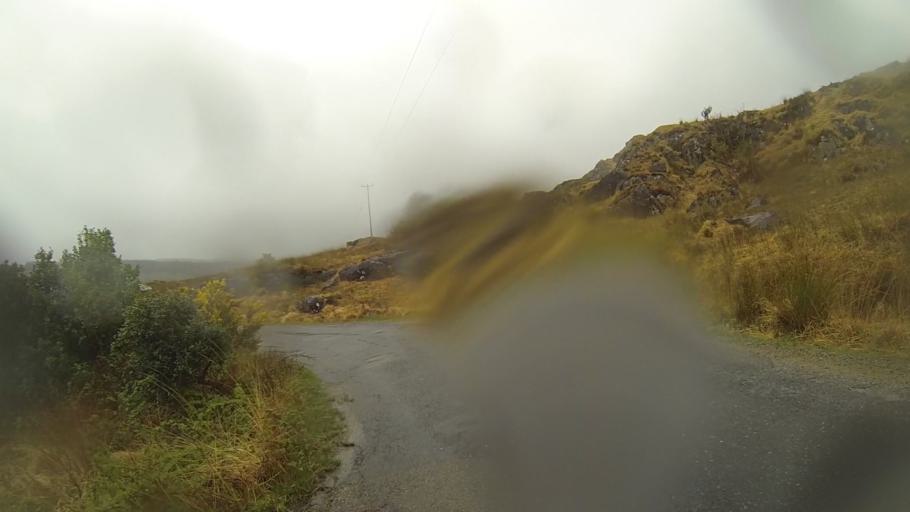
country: IE
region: Munster
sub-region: Ciarrai
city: Kenmare
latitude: 51.9599
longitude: -9.6360
